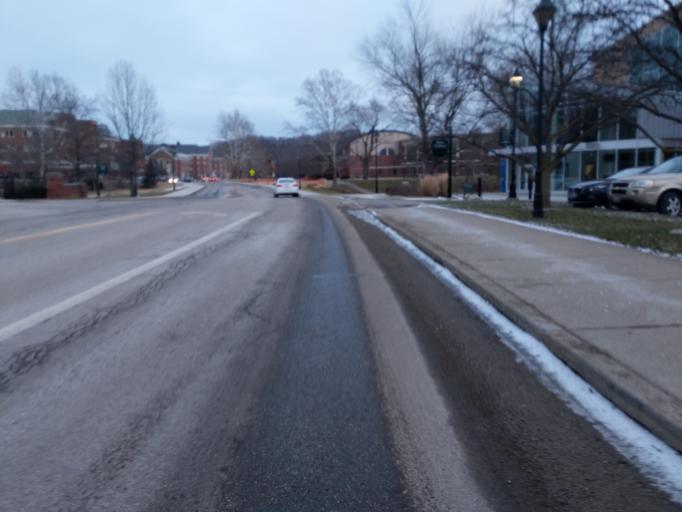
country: US
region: Ohio
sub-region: Athens County
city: Athens
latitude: 39.3219
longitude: -82.1017
